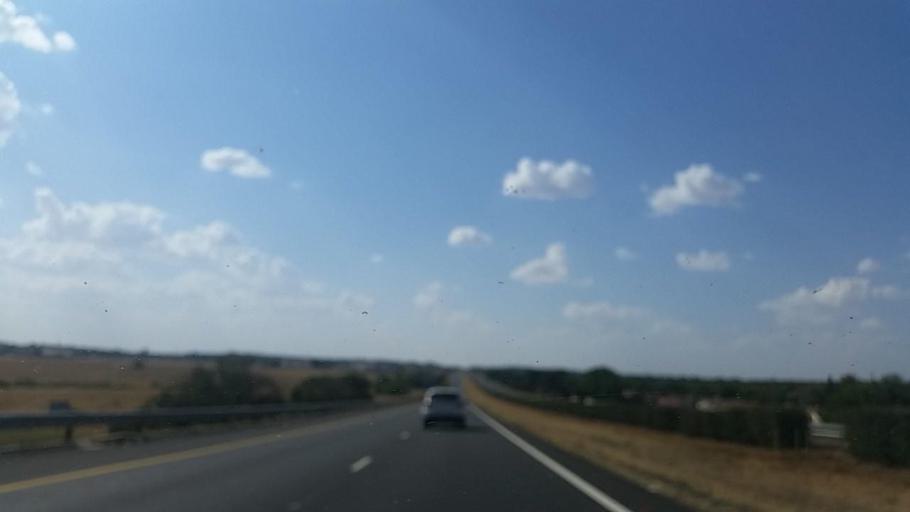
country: ZA
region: Orange Free State
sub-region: Mangaung Metropolitan Municipality
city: Bloemfontein
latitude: -29.1788
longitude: 26.1889
